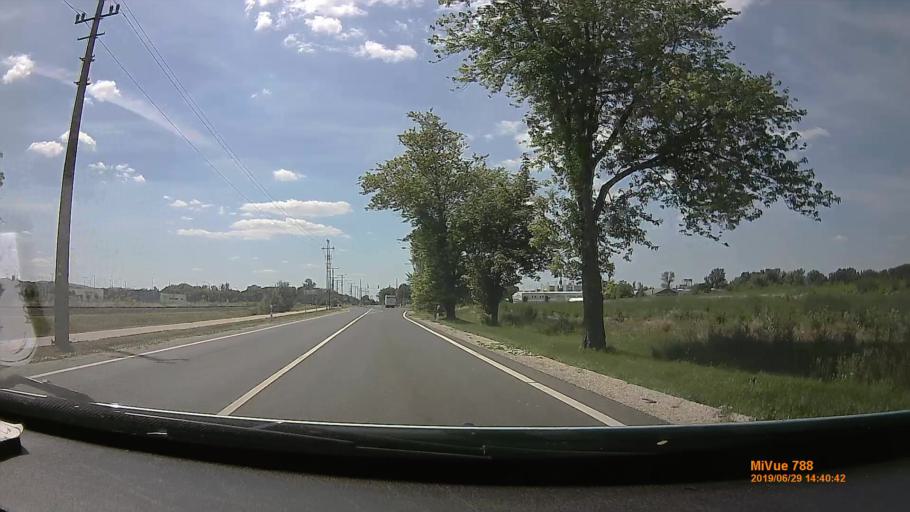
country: HU
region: Komarom-Esztergom
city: Nyergesujfalu
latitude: 47.7567
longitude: 18.5824
